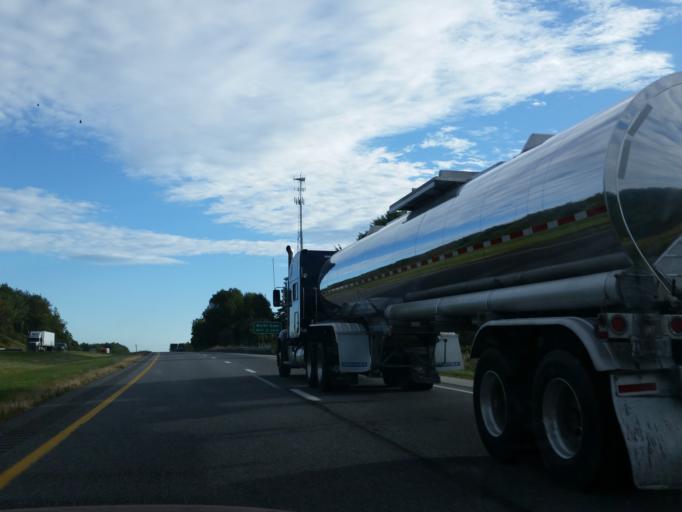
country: US
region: Pennsylvania
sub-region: Erie County
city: North East
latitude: 42.1723
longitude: -79.8467
